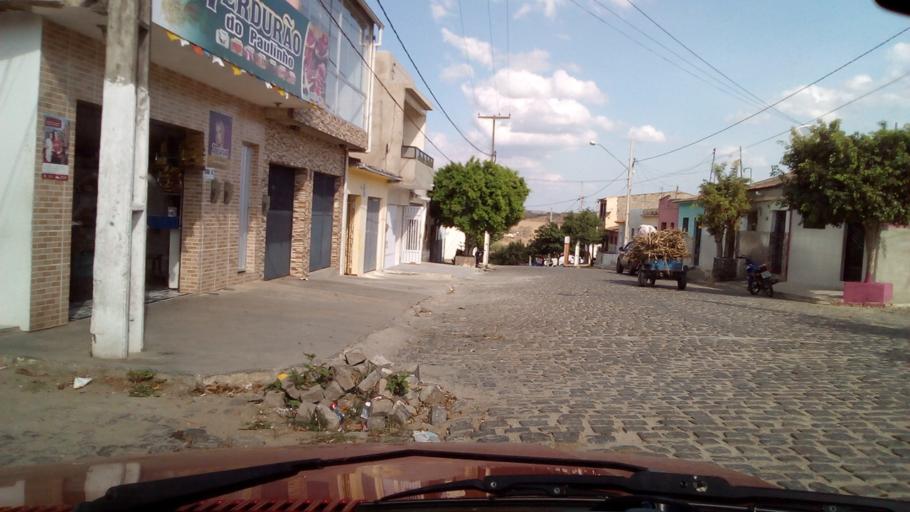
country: BR
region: Paraiba
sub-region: Arara
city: Arara
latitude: -6.8280
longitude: -35.7571
